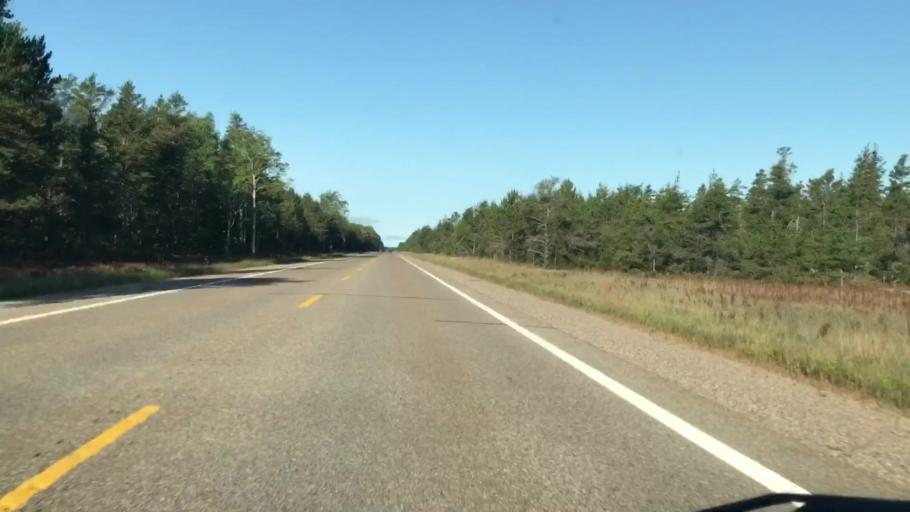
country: US
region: Michigan
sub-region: Mackinac County
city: Saint Ignace
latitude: 46.3585
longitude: -84.8468
